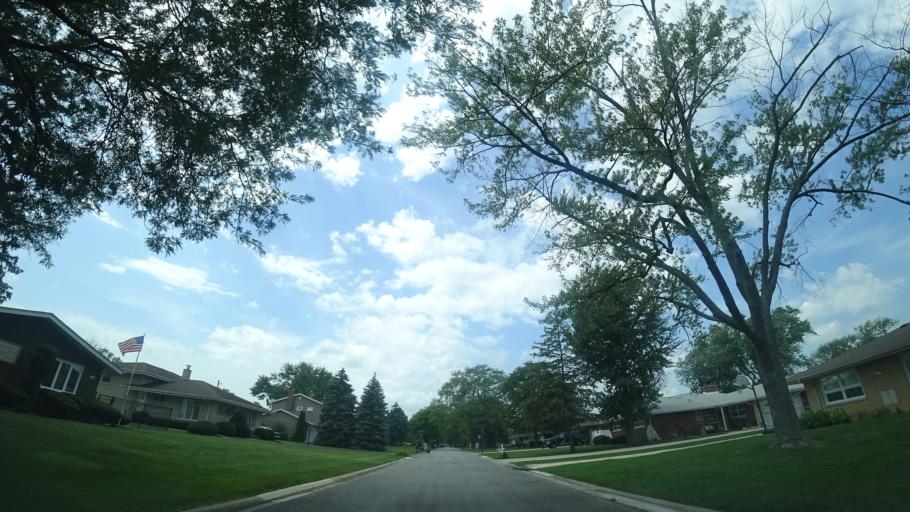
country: US
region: Illinois
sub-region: Cook County
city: Crestwood
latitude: 41.6594
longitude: -87.7693
